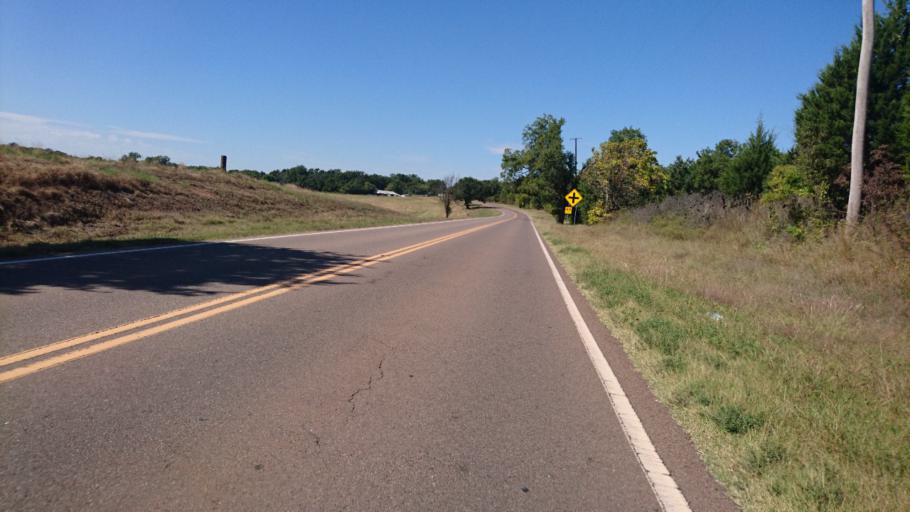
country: US
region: Oklahoma
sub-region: Oklahoma County
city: Luther
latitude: 35.6671
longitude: -97.2425
